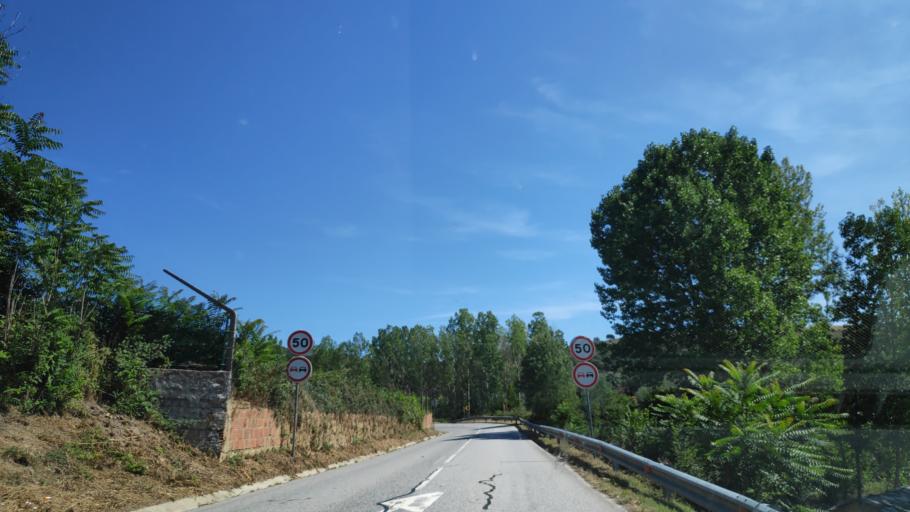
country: PT
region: Braganca
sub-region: Braganca Municipality
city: Braganca
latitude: 41.8613
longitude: -6.7463
